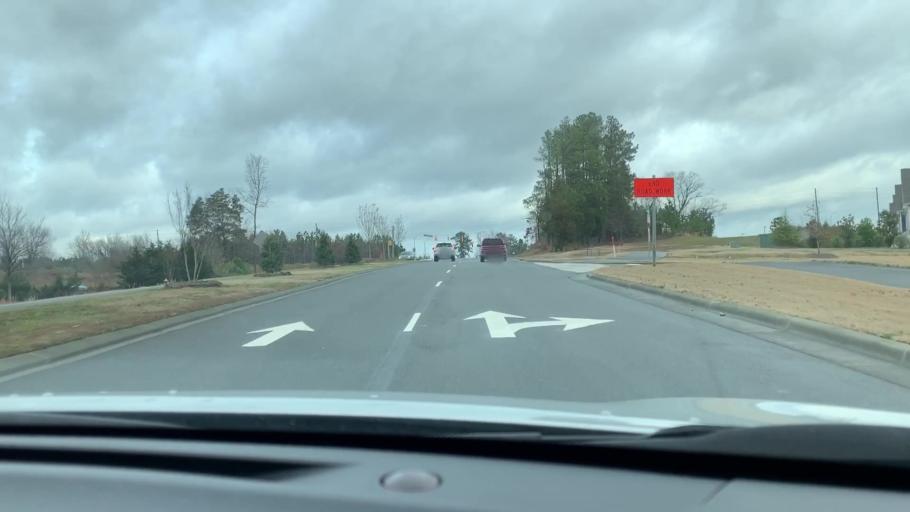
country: US
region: North Carolina
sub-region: Wake County
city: Green Level
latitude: 35.8404
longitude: -78.8997
